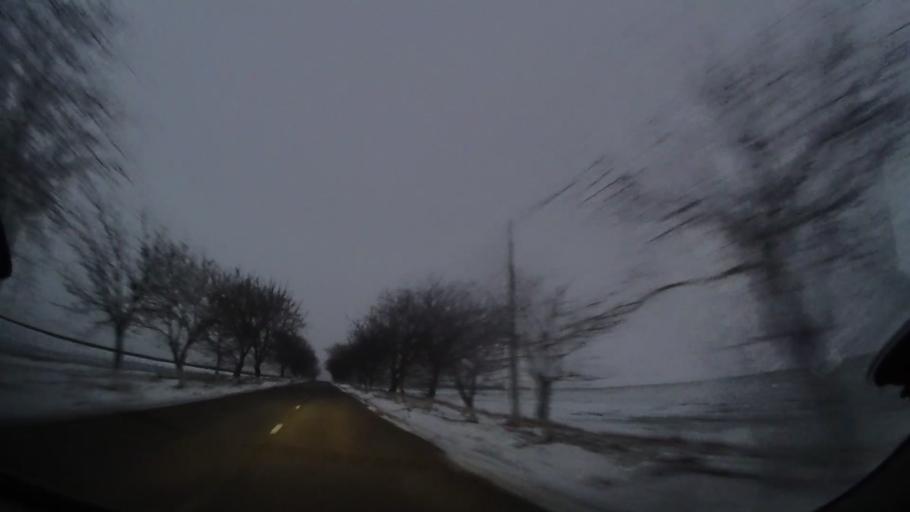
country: RO
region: Vaslui
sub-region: Comuna Dimitrie Cantemir
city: Dimitrie Cantemir
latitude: 46.5089
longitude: 28.0422
